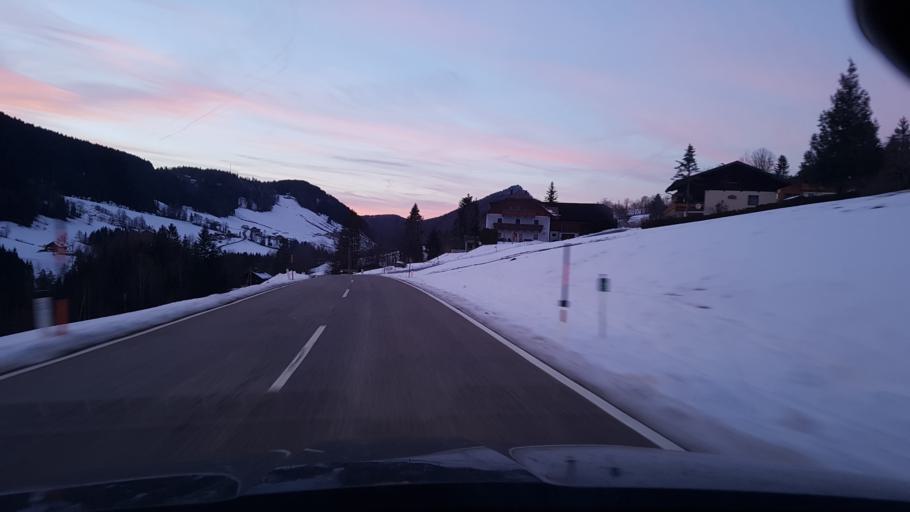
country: AT
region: Salzburg
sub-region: Politischer Bezirk Hallein
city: Krispl
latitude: 47.7053
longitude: 13.2071
